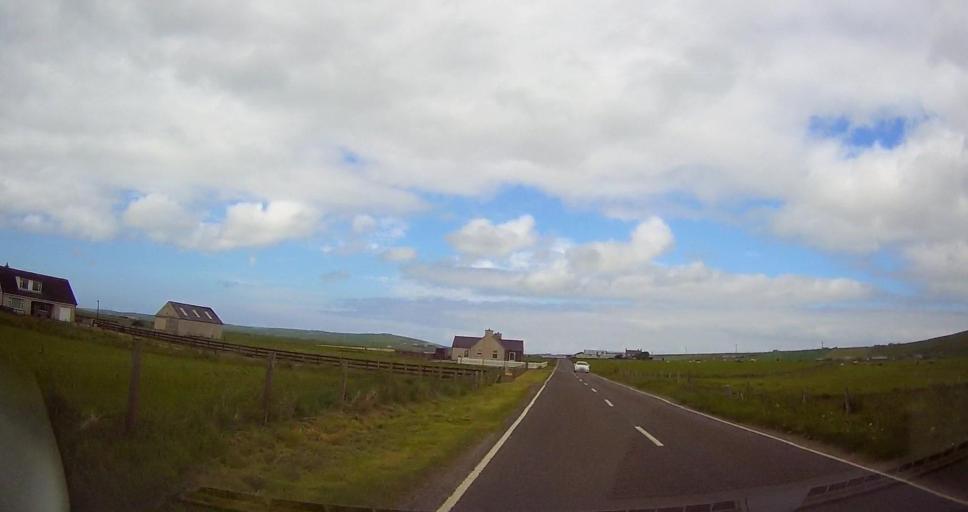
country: GB
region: Scotland
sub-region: Orkney Islands
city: Stromness
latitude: 59.0778
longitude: -3.2515
